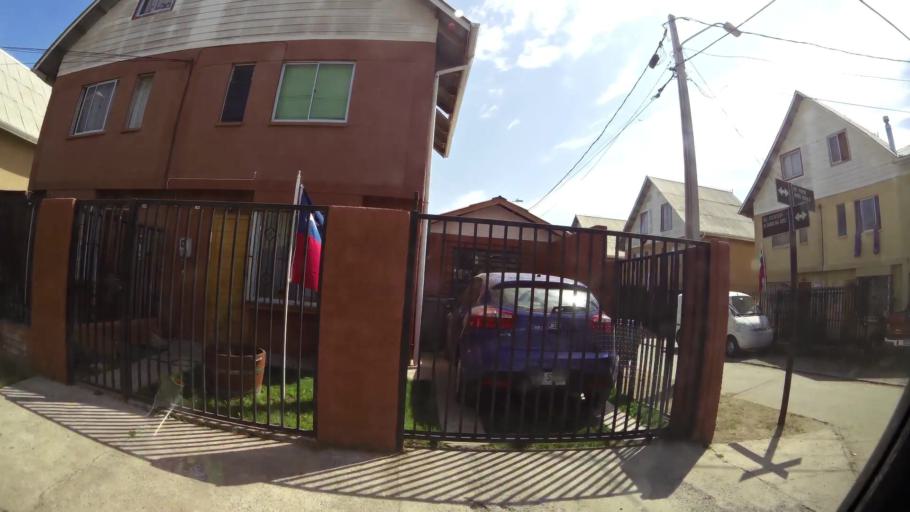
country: CL
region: Santiago Metropolitan
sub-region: Provincia de Talagante
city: Talagante
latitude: -33.6638
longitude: -70.9154
